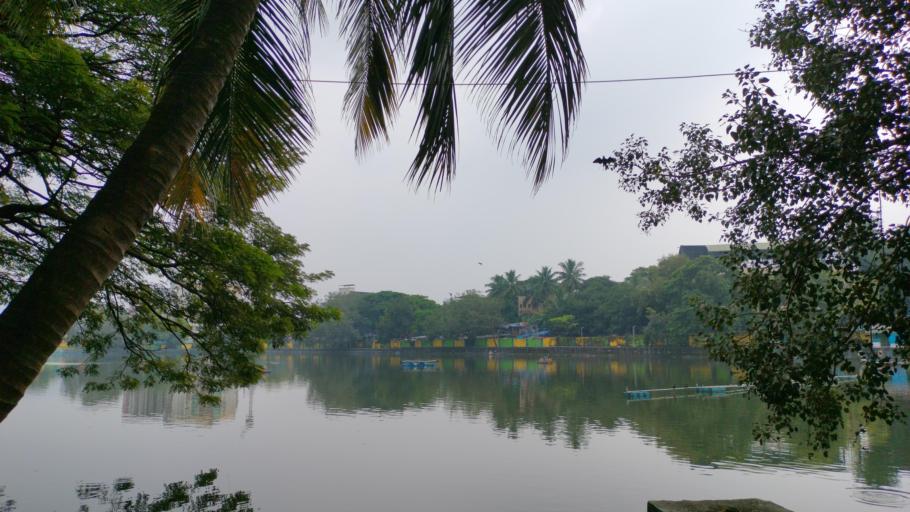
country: IN
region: Maharashtra
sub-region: Thane
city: Thane
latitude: 19.2058
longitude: 72.9784
